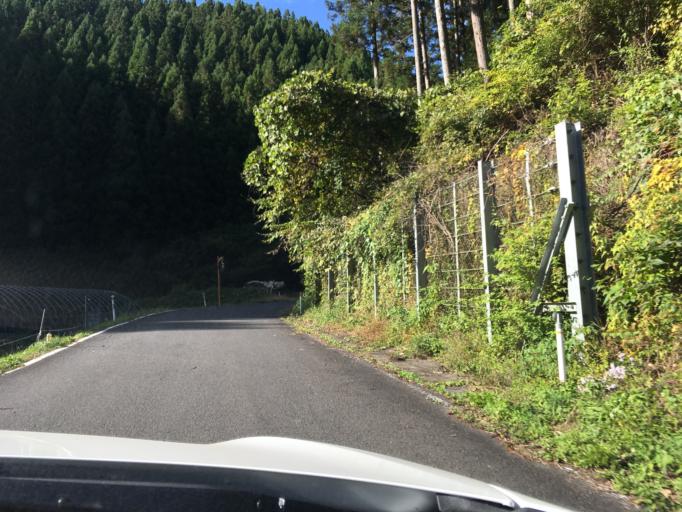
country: JP
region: Fukushima
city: Ishikawa
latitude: 37.1253
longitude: 140.5557
